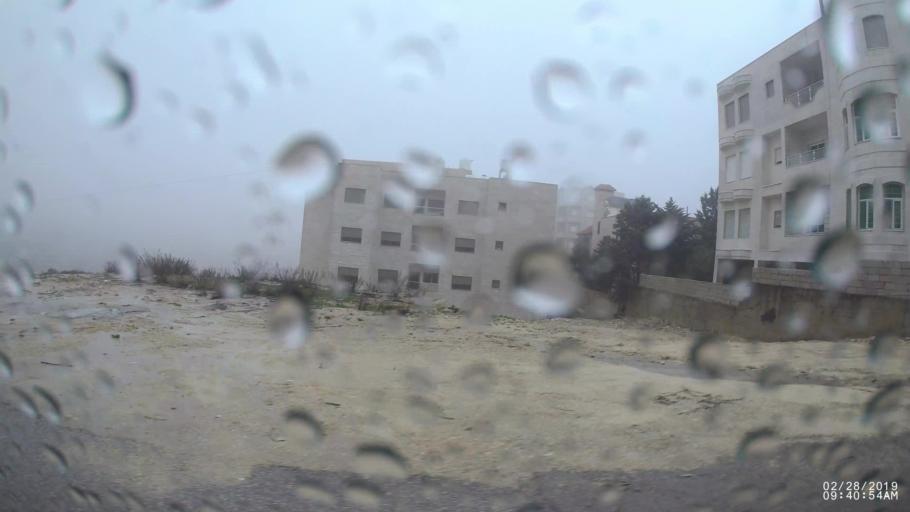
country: JO
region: Amman
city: Al Jubayhah
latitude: 32.0076
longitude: 35.8869
